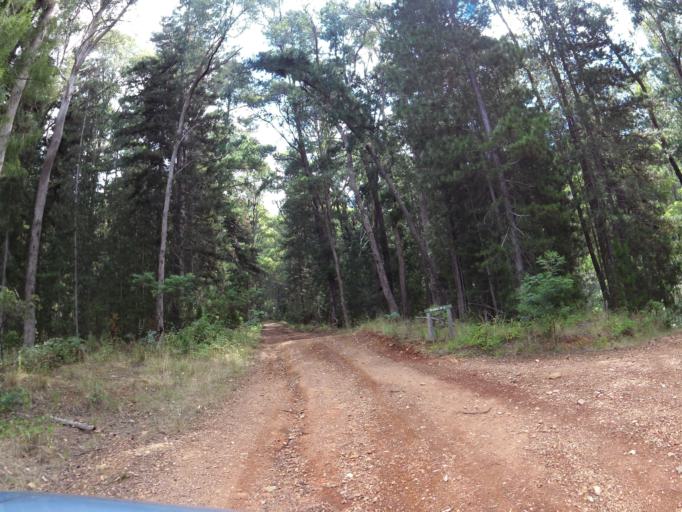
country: AU
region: Victoria
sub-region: Alpine
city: Mount Beauty
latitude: -36.7666
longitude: 147.0163
